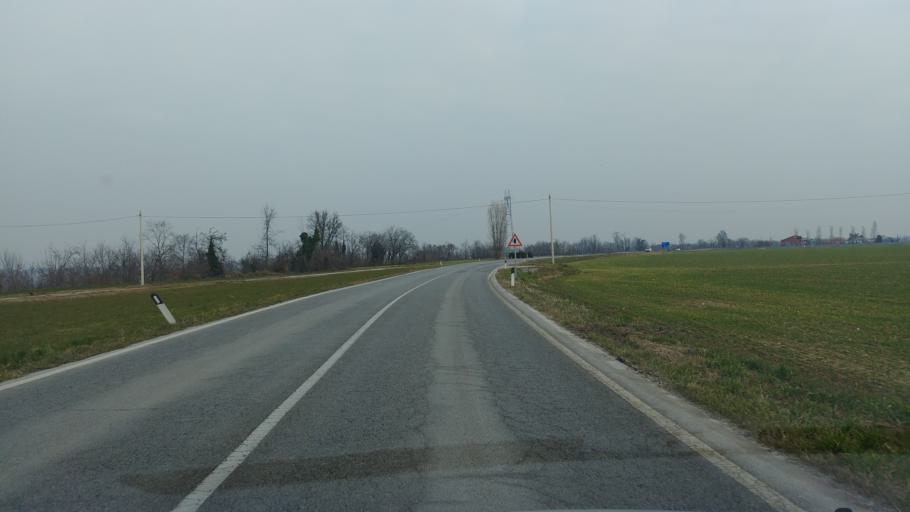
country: IT
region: Piedmont
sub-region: Provincia di Cuneo
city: Montanera
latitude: 44.4779
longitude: 7.6837
